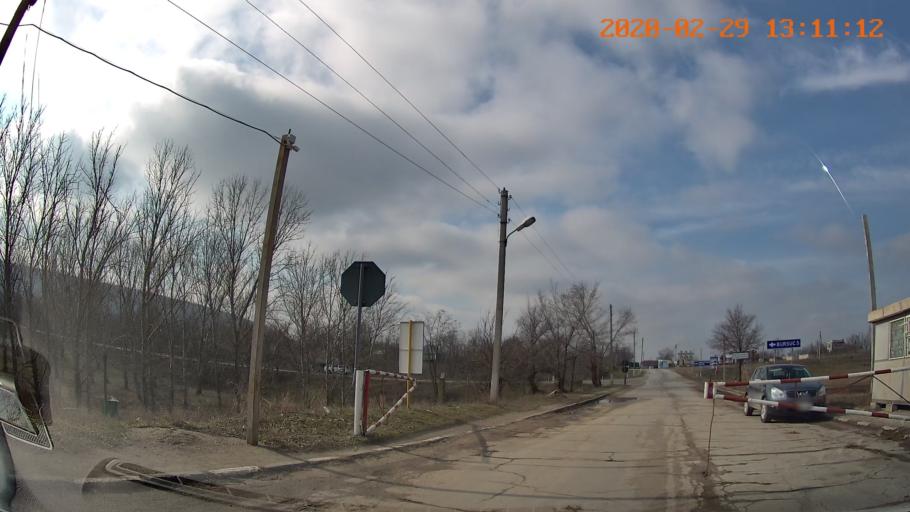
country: MD
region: Telenesti
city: Camenca
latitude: 48.0123
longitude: 28.6999
